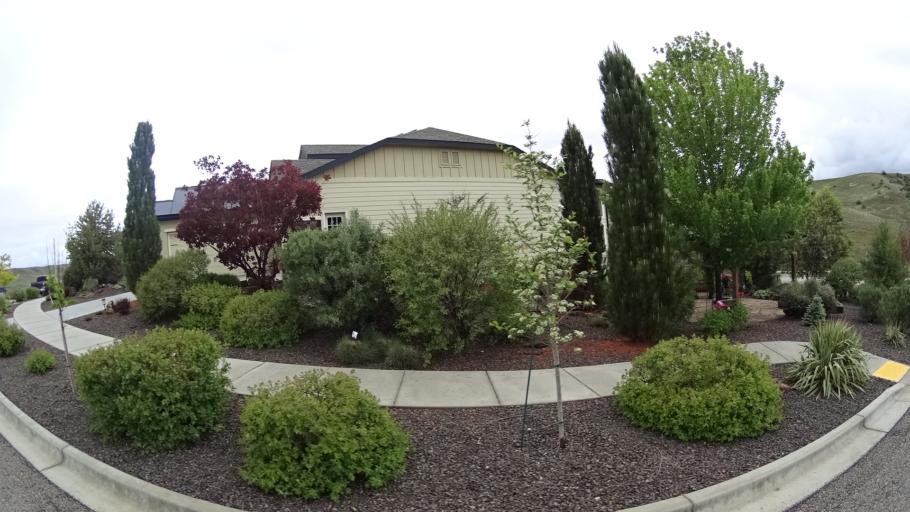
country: US
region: Idaho
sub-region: Ada County
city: Eagle
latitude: 43.7678
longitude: -116.2579
